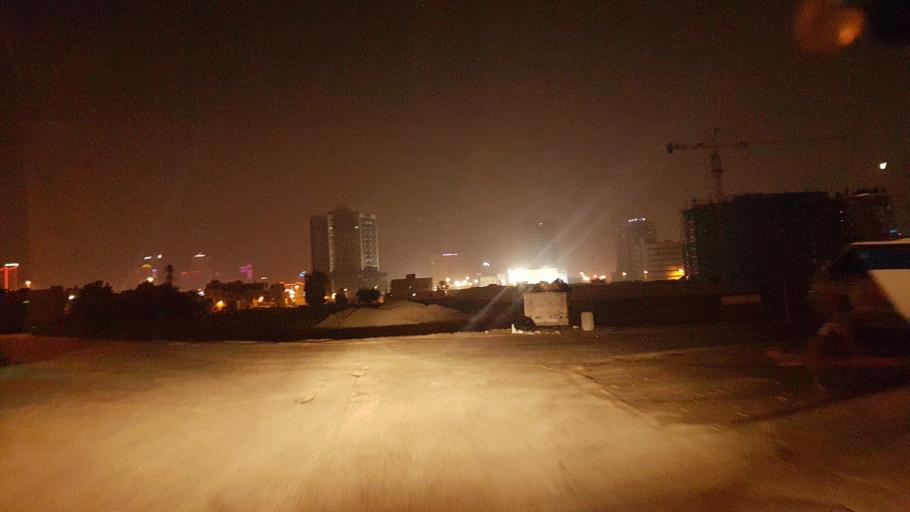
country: BH
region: Manama
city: Jidd Hafs
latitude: 26.2227
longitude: 50.5392
